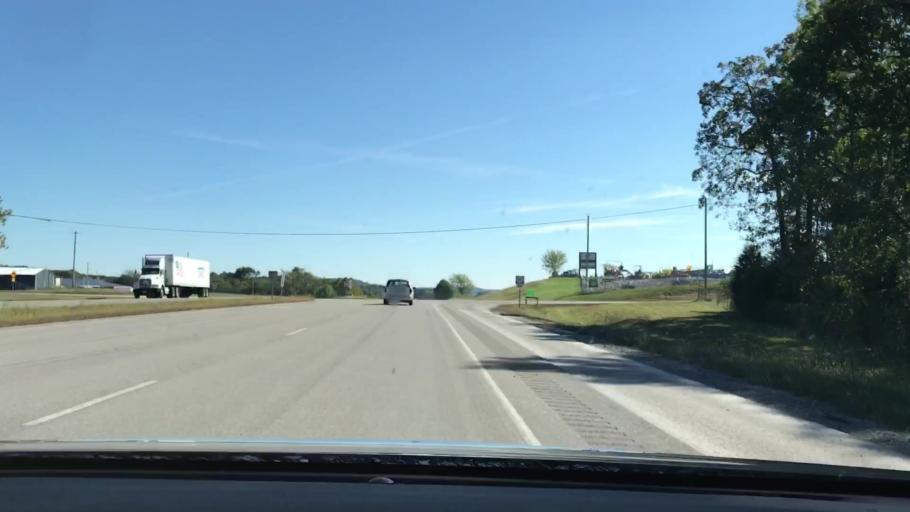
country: US
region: Kentucky
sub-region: Todd County
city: Elkton
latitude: 36.8473
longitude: -87.3124
